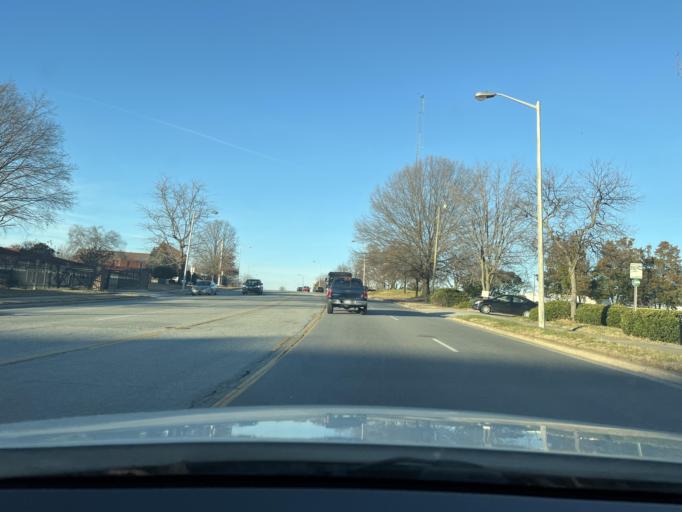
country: US
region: North Carolina
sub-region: Guilford County
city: Greensboro
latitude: 36.0601
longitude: -79.7933
